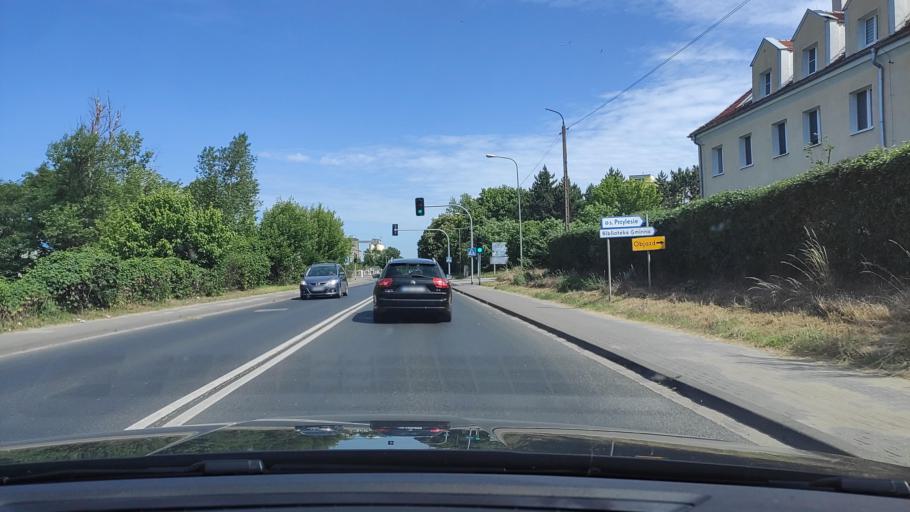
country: PL
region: Greater Poland Voivodeship
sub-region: Powiat poznanski
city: Czerwonak
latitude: 52.4795
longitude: 16.9788
